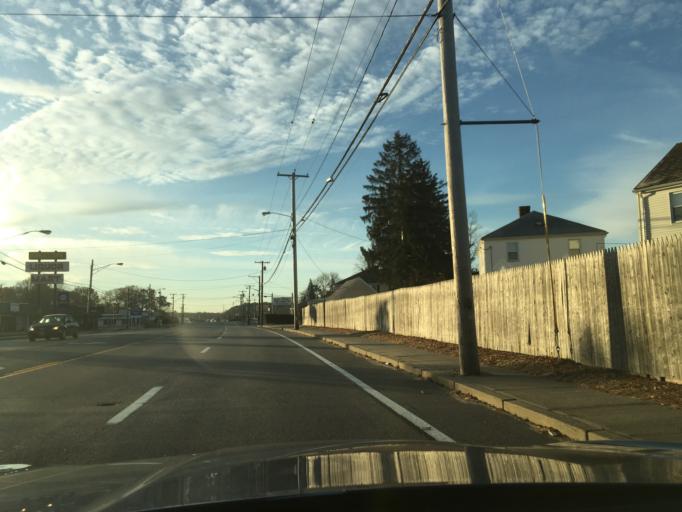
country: US
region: Rhode Island
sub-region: Kent County
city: East Greenwich
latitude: 41.6132
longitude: -71.4577
